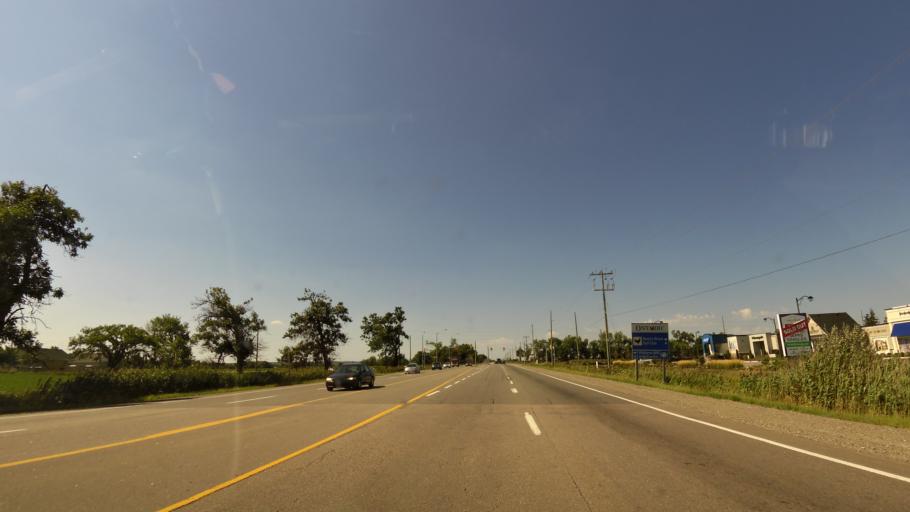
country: CA
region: Ontario
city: Brampton
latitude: 43.7526
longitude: -79.8501
